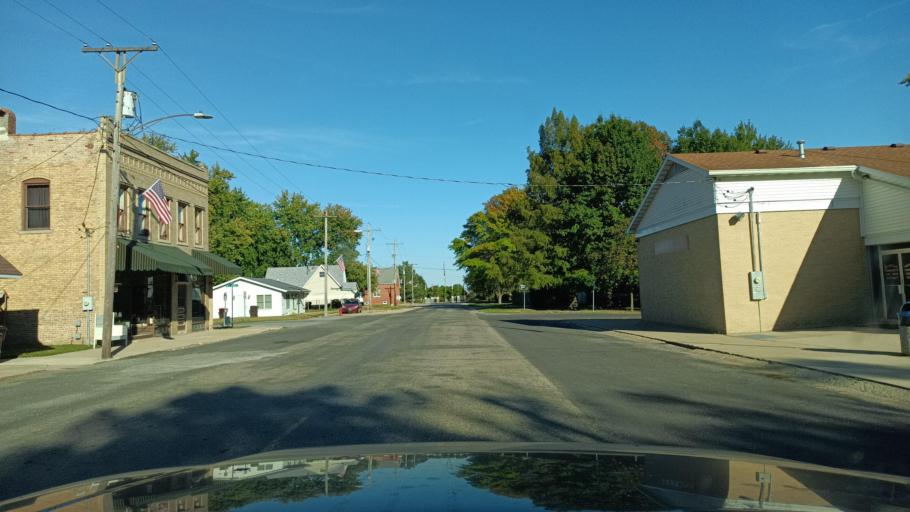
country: US
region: Illinois
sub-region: De Witt County
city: Clinton
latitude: 40.2207
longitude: -88.9611
